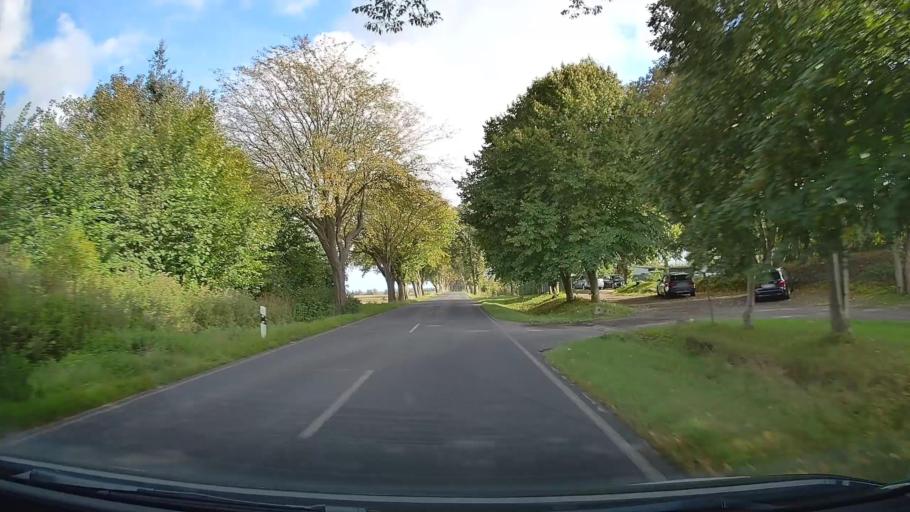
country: DE
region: Mecklenburg-Vorpommern
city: Bergen auf Ruegen
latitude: 54.4065
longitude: 13.4470
